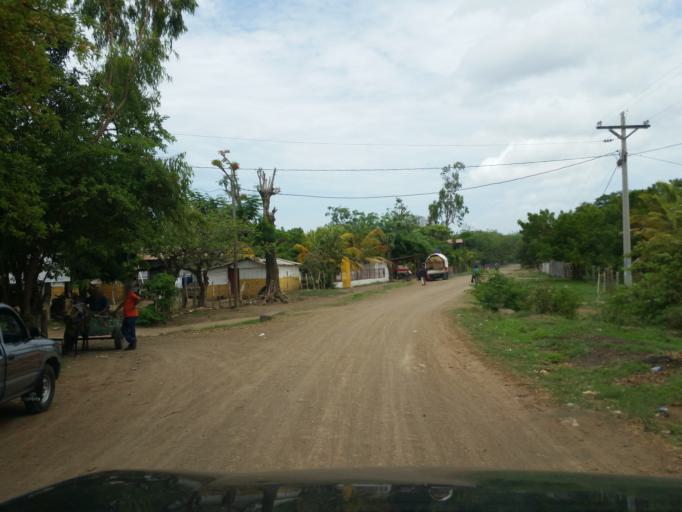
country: NI
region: Granada
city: Nandaime
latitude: 11.6537
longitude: -85.9752
